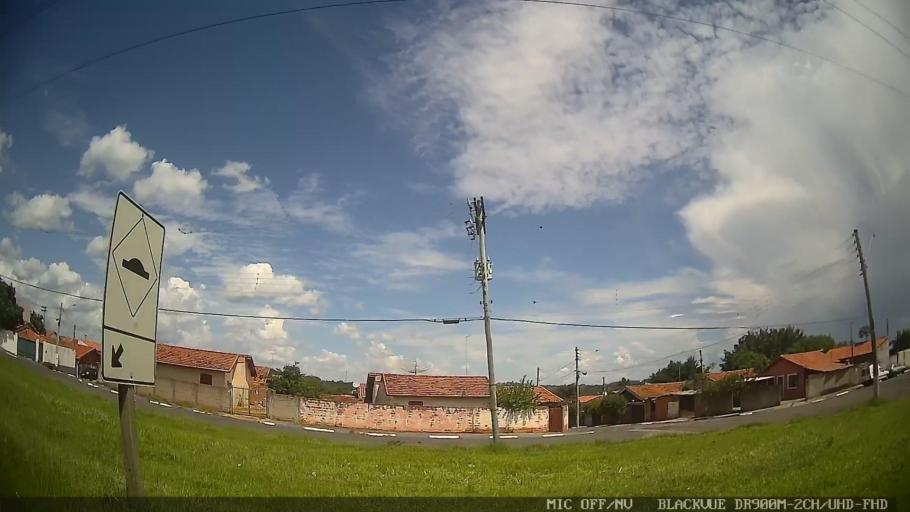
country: BR
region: Sao Paulo
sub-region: Conchas
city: Conchas
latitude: -23.0399
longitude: -48.0201
